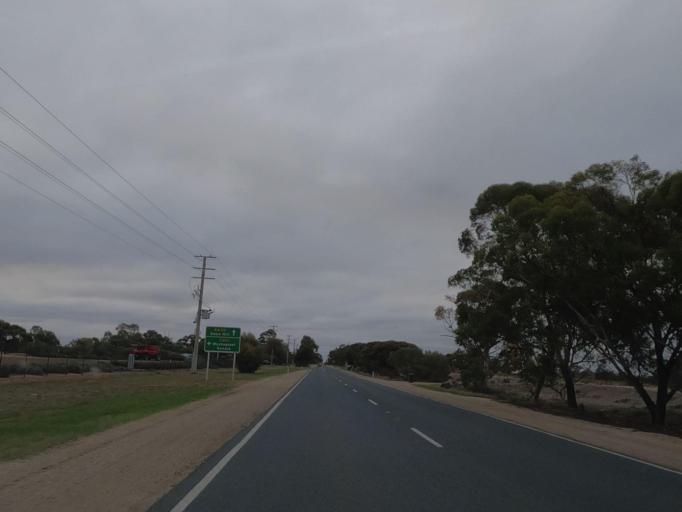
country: AU
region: Victoria
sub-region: Swan Hill
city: Swan Hill
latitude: -35.3875
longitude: 143.5682
